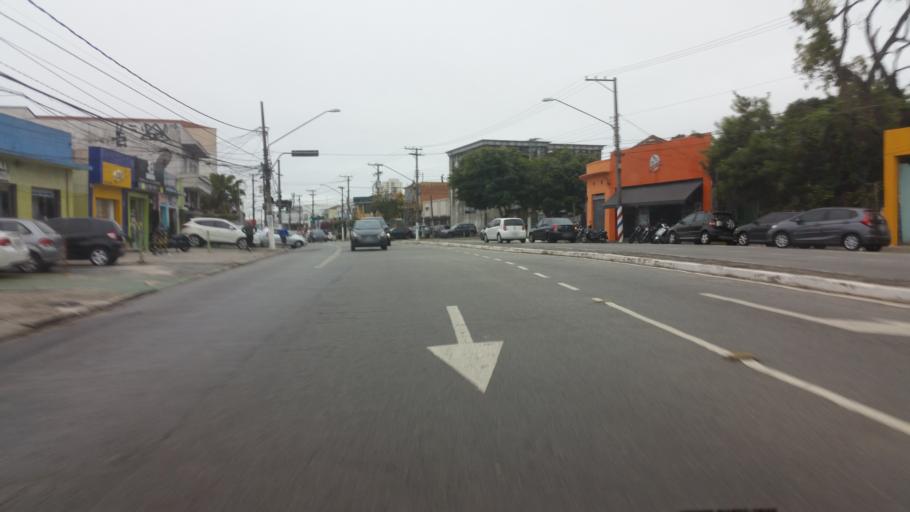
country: BR
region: Sao Paulo
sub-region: Sao Caetano Do Sul
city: Sao Caetano do Sul
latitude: -23.6178
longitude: -46.6184
